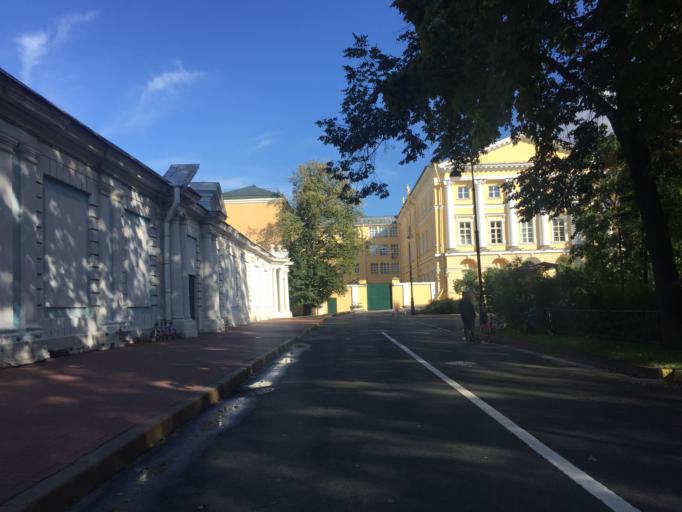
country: RU
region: Leningrad
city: Finlyandskiy
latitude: 59.9474
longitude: 30.3943
